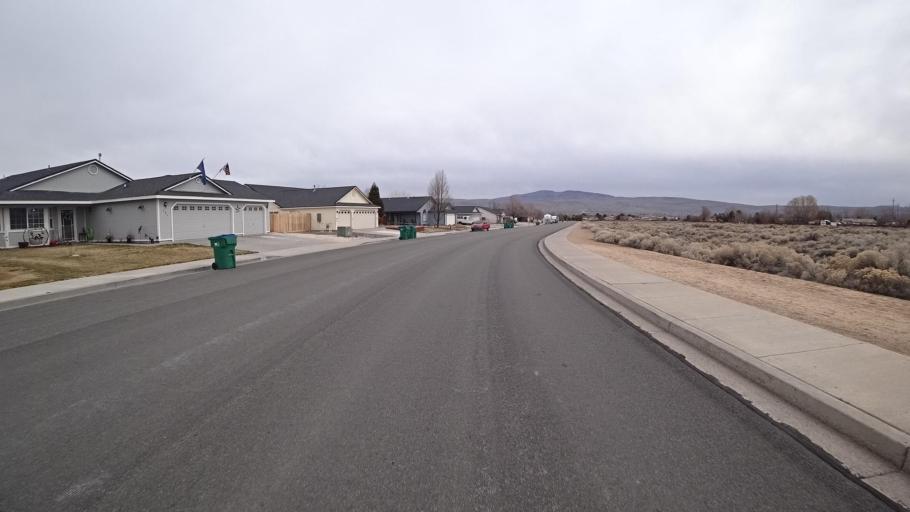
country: US
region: Nevada
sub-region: Washoe County
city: Spanish Springs
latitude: 39.6362
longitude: -119.7248
